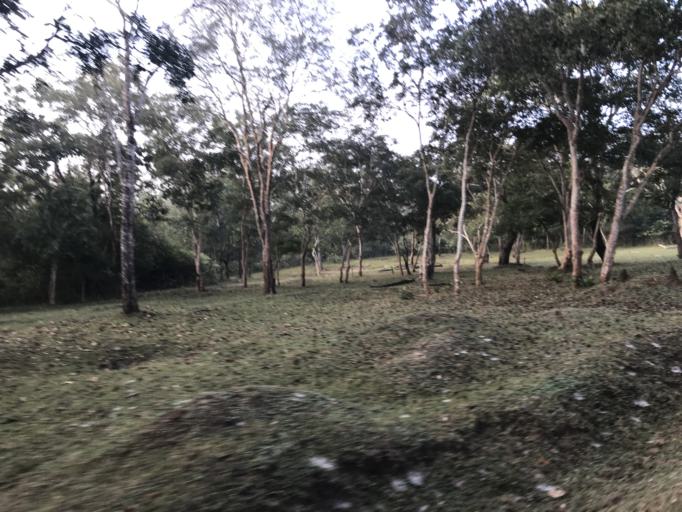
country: IN
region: Karnataka
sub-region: Mysore
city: Heggadadevankote
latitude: 12.0060
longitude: 76.2333
